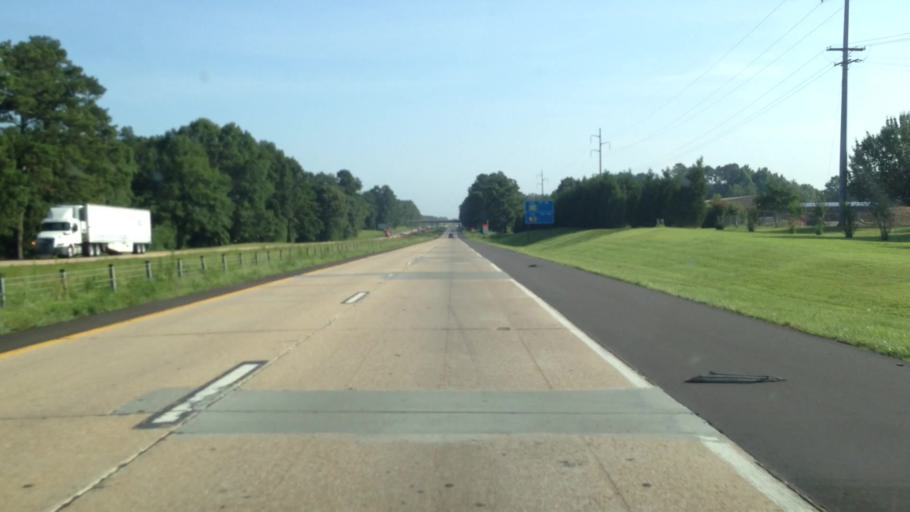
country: US
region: Mississippi
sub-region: Pike County
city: Summit
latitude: 31.2658
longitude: -90.4790
